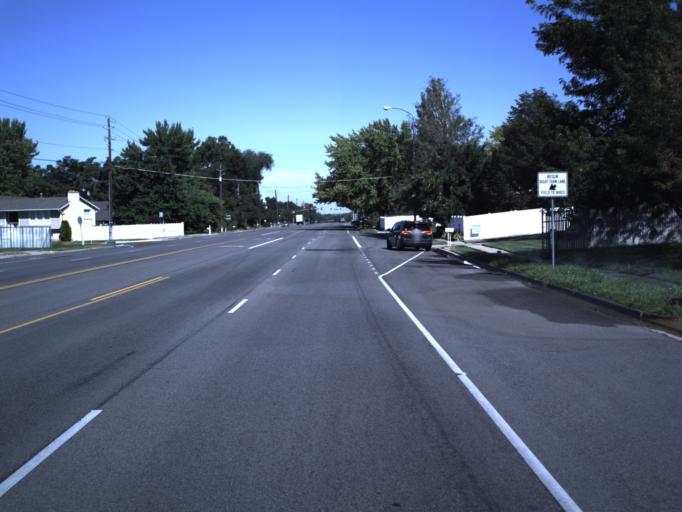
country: US
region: Utah
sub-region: Davis County
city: Kaysville
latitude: 41.0235
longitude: -111.9269
